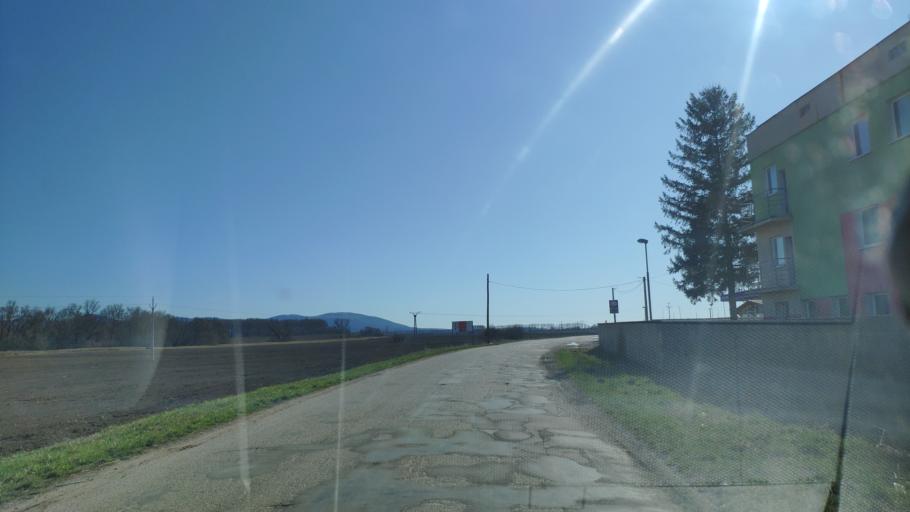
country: SK
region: Kosicky
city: Kosice
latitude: 48.6009
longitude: 21.3216
